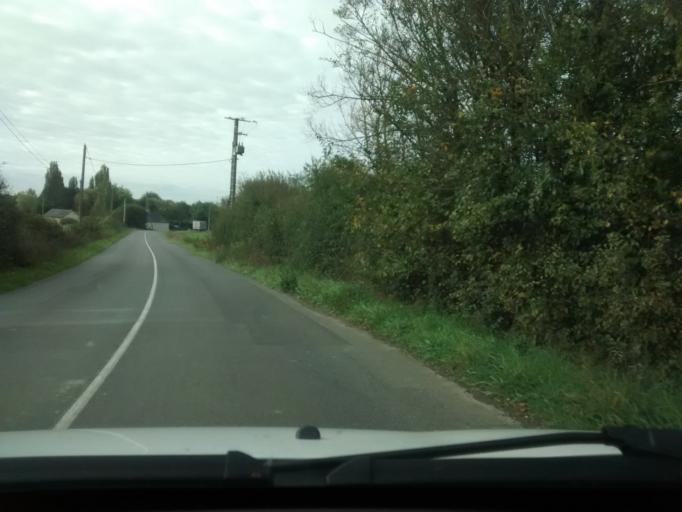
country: FR
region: Brittany
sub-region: Departement d'Ille-et-Vilaine
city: Chavagne
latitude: 48.0799
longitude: -1.7580
